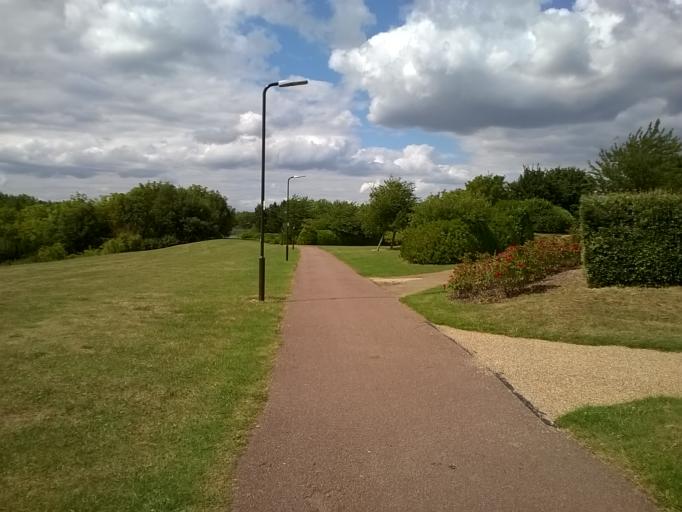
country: GB
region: England
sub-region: Milton Keynes
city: Milton Keynes
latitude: 52.0460
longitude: -0.7474
